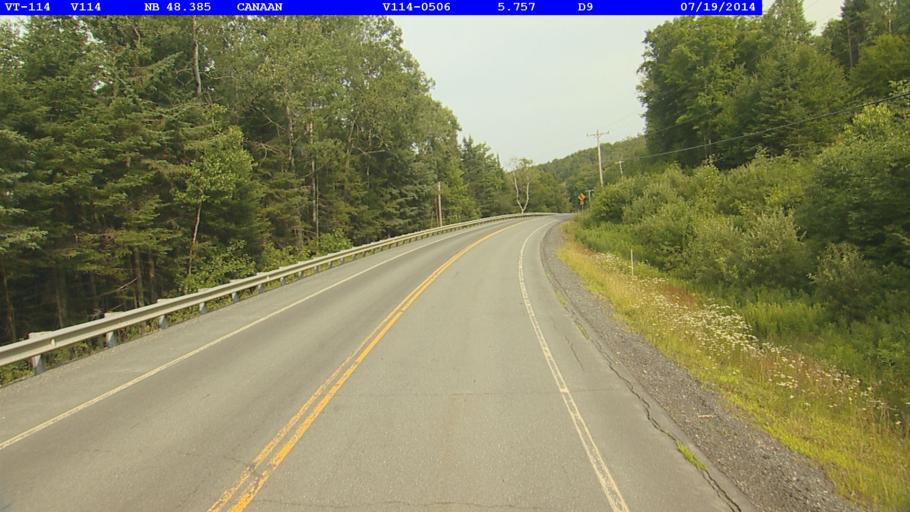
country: US
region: New Hampshire
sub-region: Coos County
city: Colebrook
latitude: 45.0095
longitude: -71.5805
